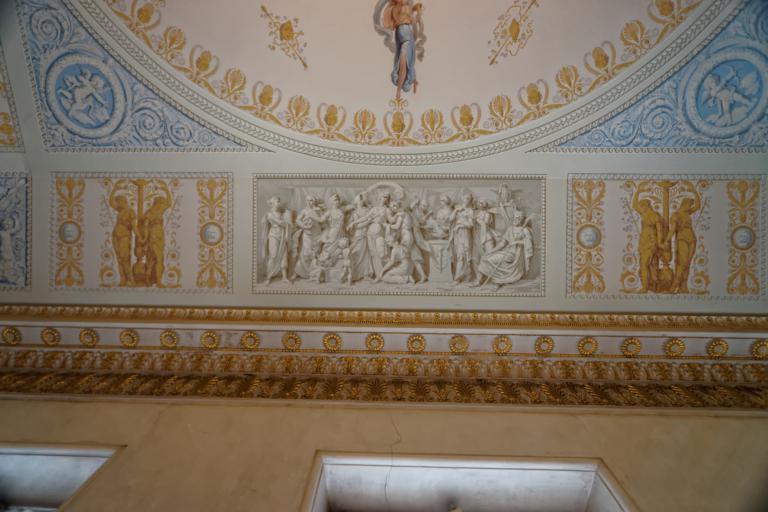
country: RU
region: Leningrad
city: Krestovskiy ostrov
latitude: 59.9792
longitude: 30.2701
